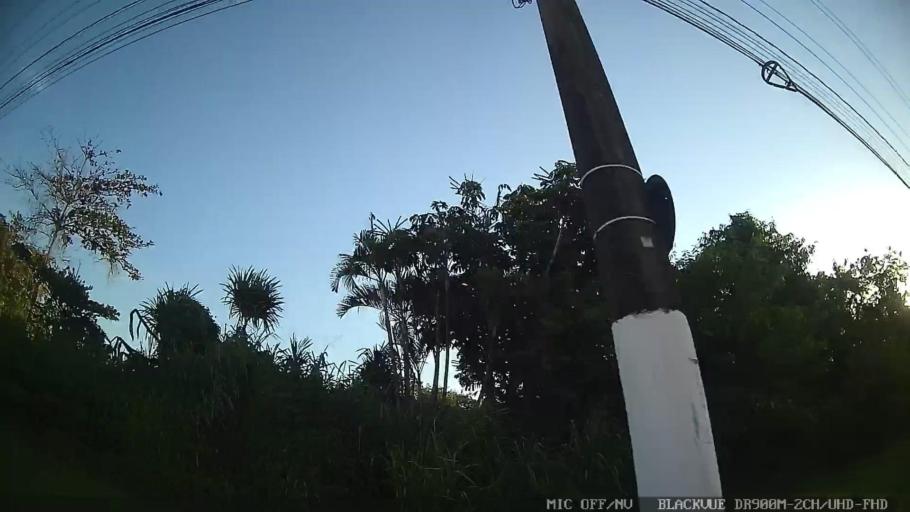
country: BR
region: Sao Paulo
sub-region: Guaruja
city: Guaruja
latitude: -23.9799
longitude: -46.2699
